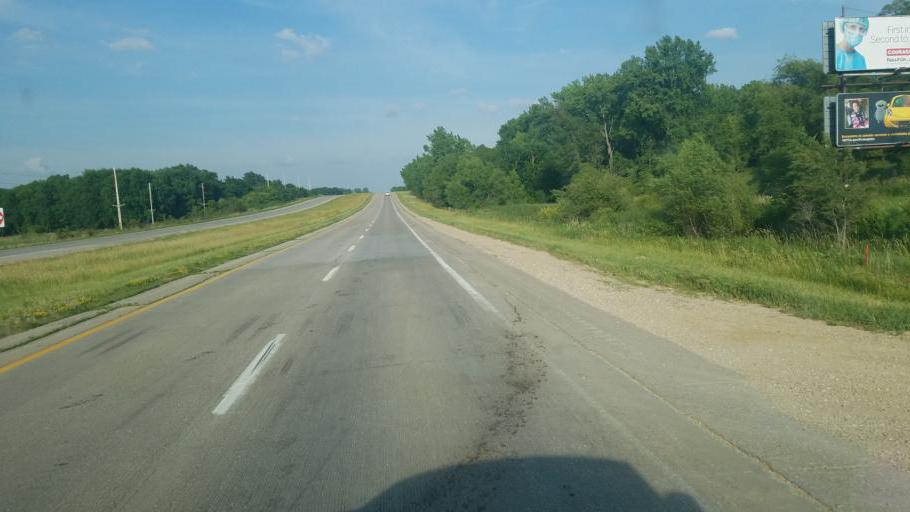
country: US
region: Iowa
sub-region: Marshall County
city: Marshalltown
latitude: 42.0062
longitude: -92.7608
